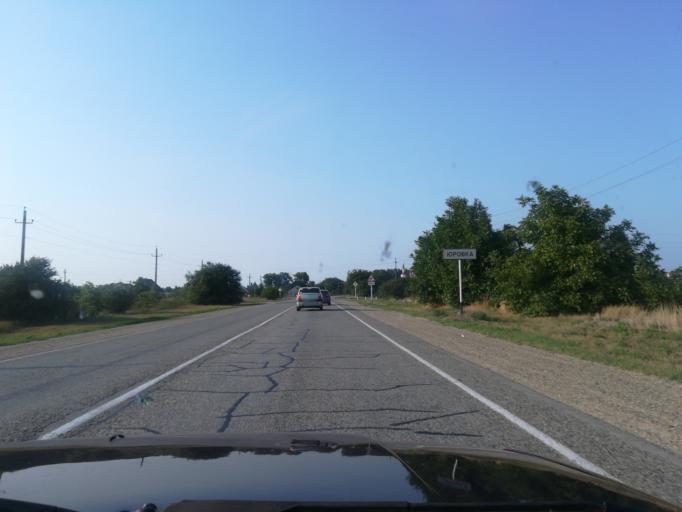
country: RU
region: Krasnodarskiy
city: Yurovka
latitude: 45.1092
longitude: 37.4219
